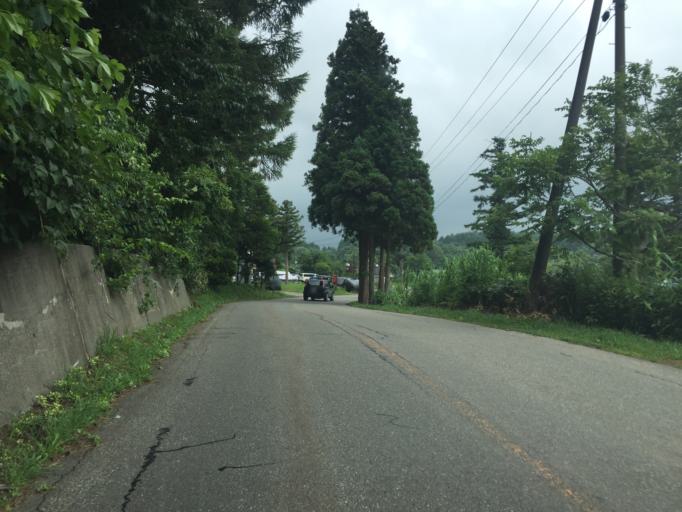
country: JP
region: Fukushima
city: Inawashiro
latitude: 37.6847
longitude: 140.0656
